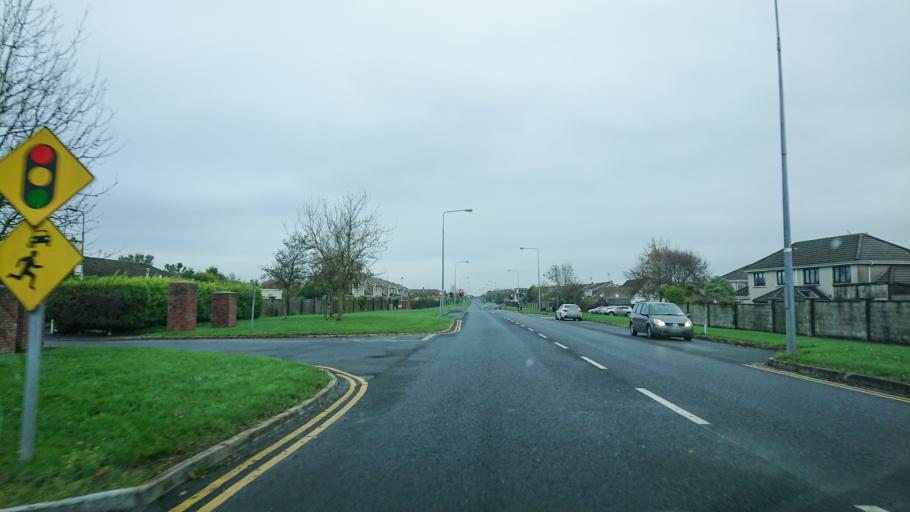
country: IE
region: Munster
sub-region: Waterford
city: Tra Mhor
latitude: 52.1603
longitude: -7.1682
